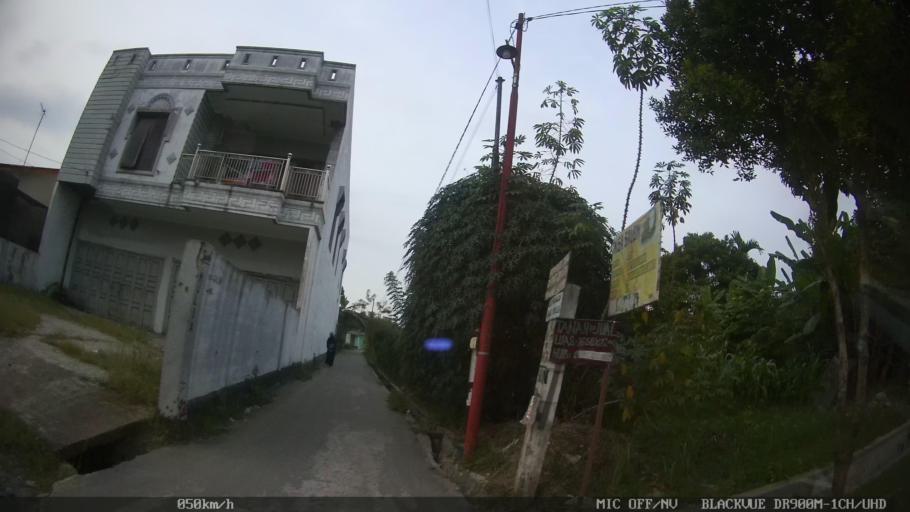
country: ID
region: North Sumatra
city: Sunggal
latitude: 3.5820
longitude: 98.6023
